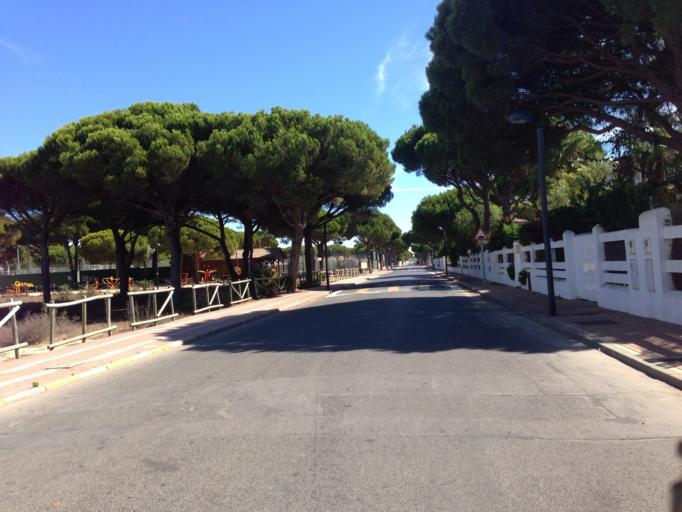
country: ES
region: Andalusia
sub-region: Provincia de Cadiz
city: Conil de la Frontera
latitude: 36.3157
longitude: -6.1510
